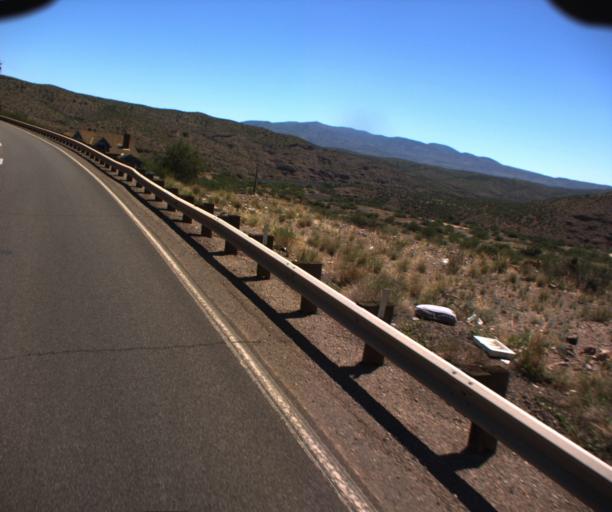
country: US
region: Arizona
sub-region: Greenlee County
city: Clifton
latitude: 33.0303
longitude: -109.2993
